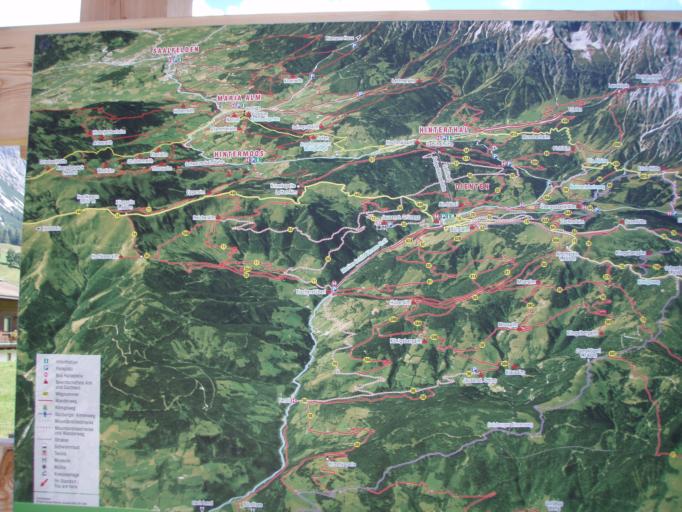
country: AT
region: Salzburg
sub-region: Politischer Bezirk Zell am See
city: Dienten am Hochkonig
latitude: 47.3857
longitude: 13.0127
